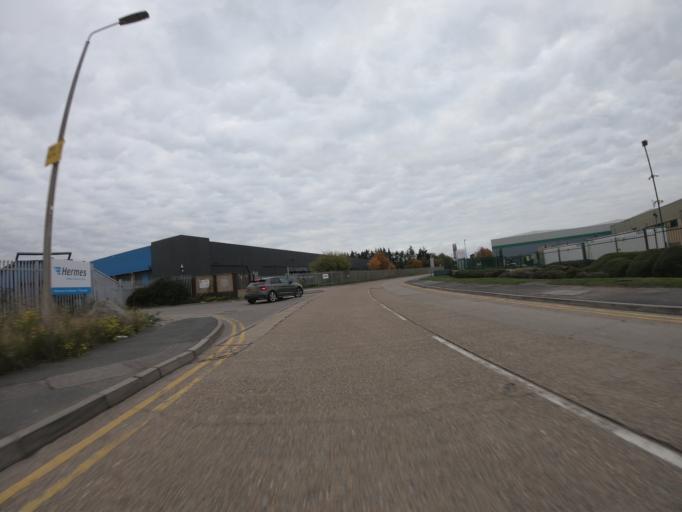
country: GB
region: England
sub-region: Kent
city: West Thurrock
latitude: 51.4813
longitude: 0.2689
